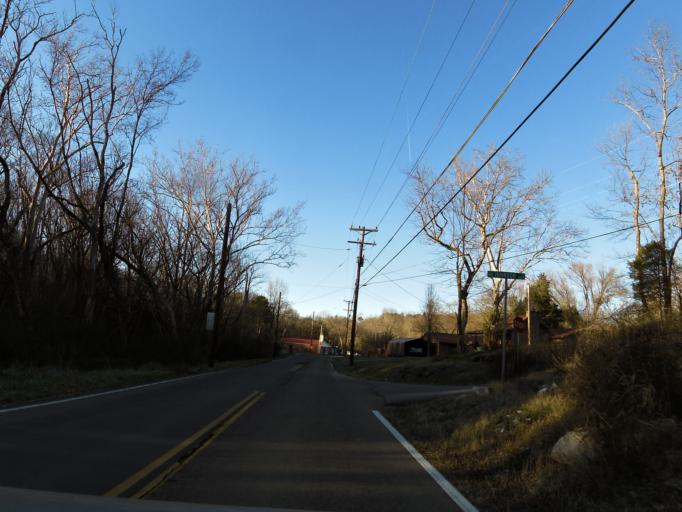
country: US
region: Tennessee
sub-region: Knox County
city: Knoxville
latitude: 35.9496
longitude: -83.8644
